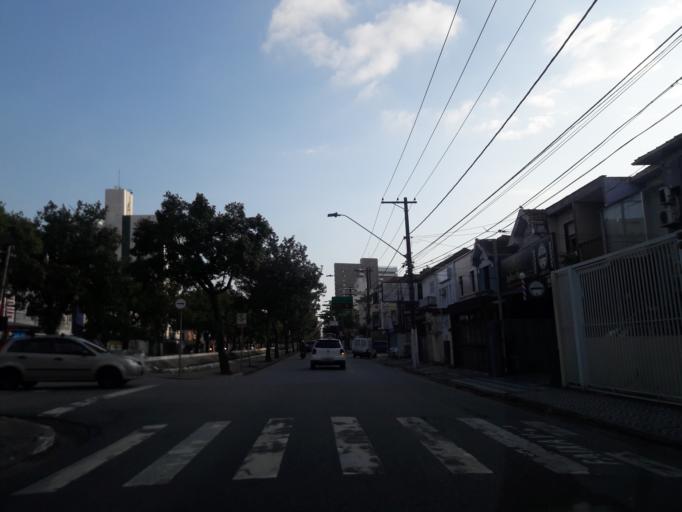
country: BR
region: Sao Paulo
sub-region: Santos
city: Santos
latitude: -23.9515
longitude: -46.3372
